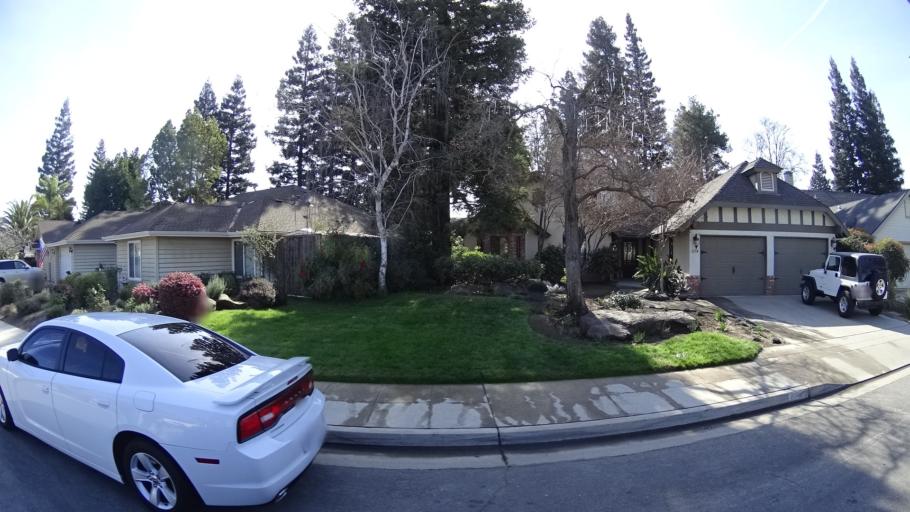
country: US
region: California
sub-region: Fresno County
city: Clovis
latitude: 36.8839
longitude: -119.7738
